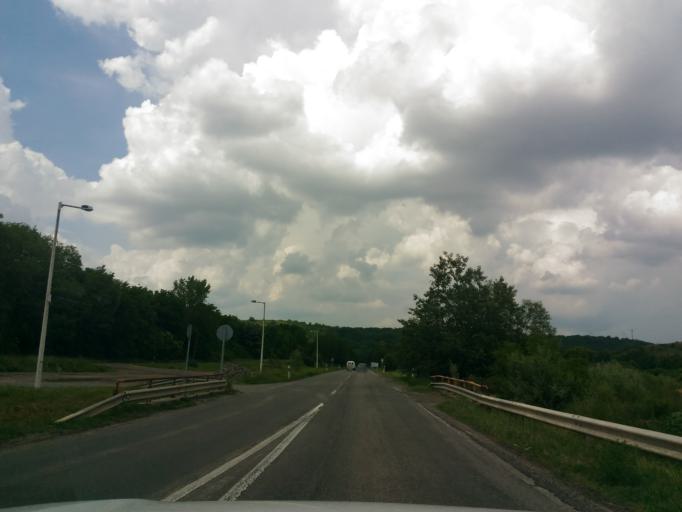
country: HU
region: Baranya
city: Mecseknadasd
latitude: 46.2409
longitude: 18.4795
